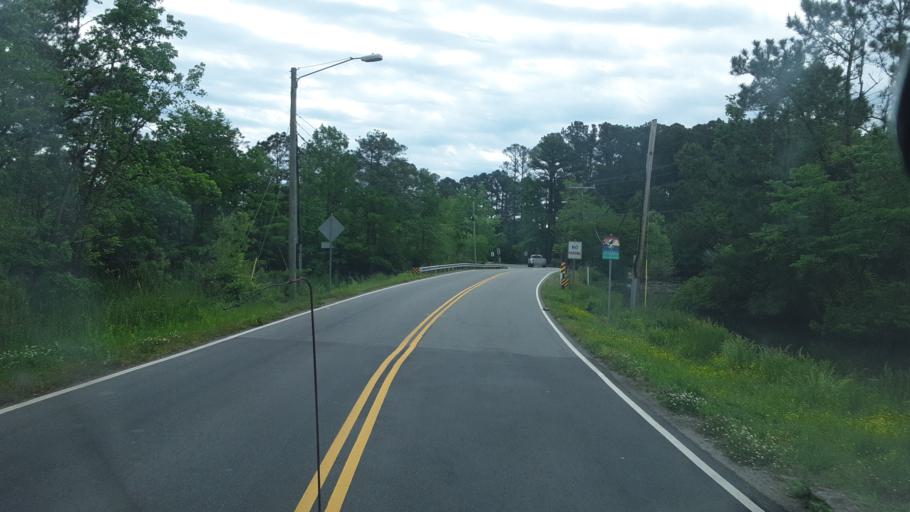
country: US
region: Virginia
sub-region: City of Virginia Beach
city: Virginia Beach
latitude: 36.7322
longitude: -75.9854
